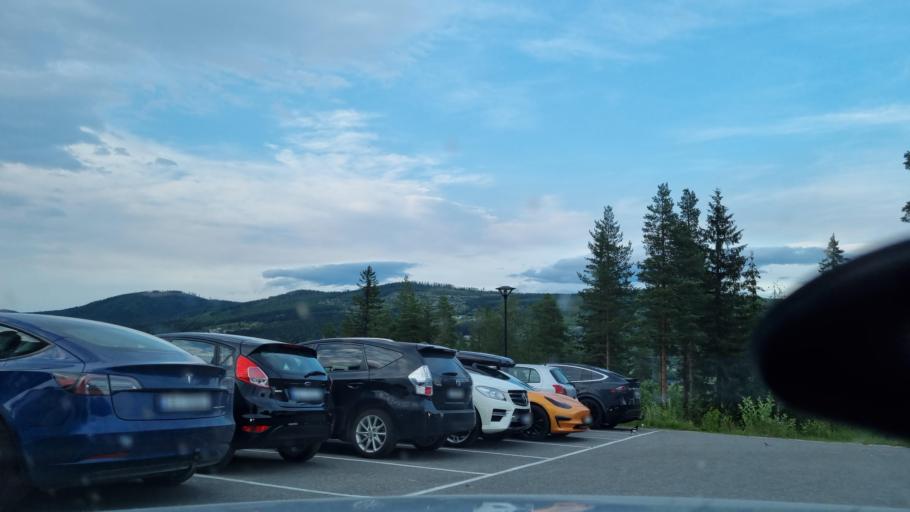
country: NO
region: Hedmark
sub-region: Trysil
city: Innbygda
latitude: 61.3071
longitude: 12.2450
